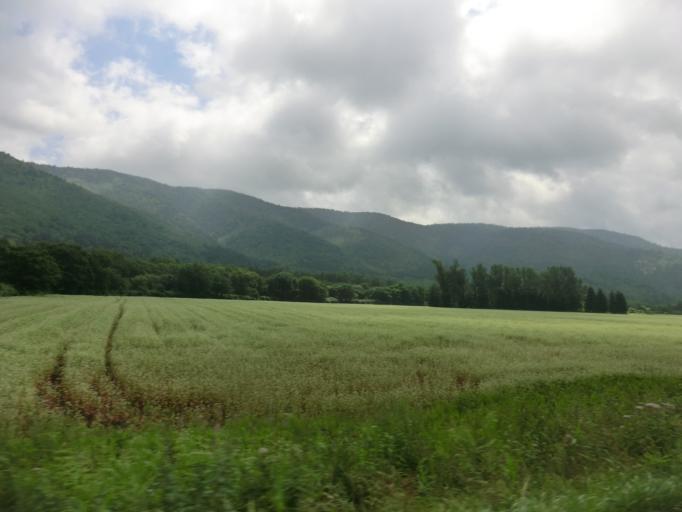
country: JP
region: Hokkaido
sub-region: Asahikawa-shi
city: Asahikawa
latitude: 44.0931
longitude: 142.1493
